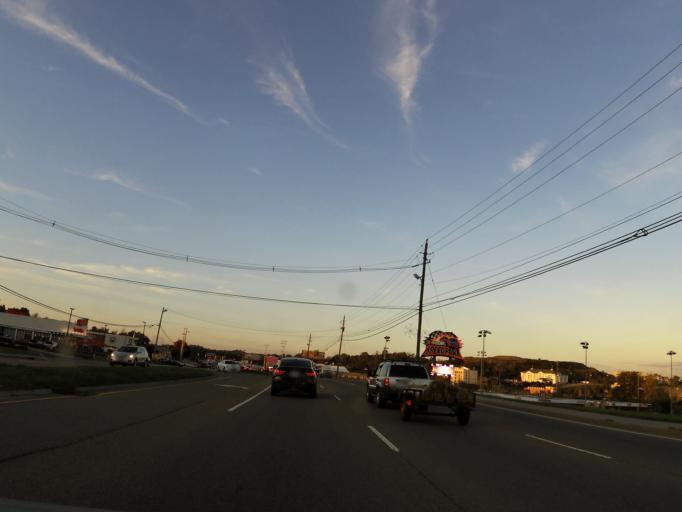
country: US
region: Tennessee
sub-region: Sevier County
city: Sevierville
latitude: 35.8357
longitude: -83.5718
